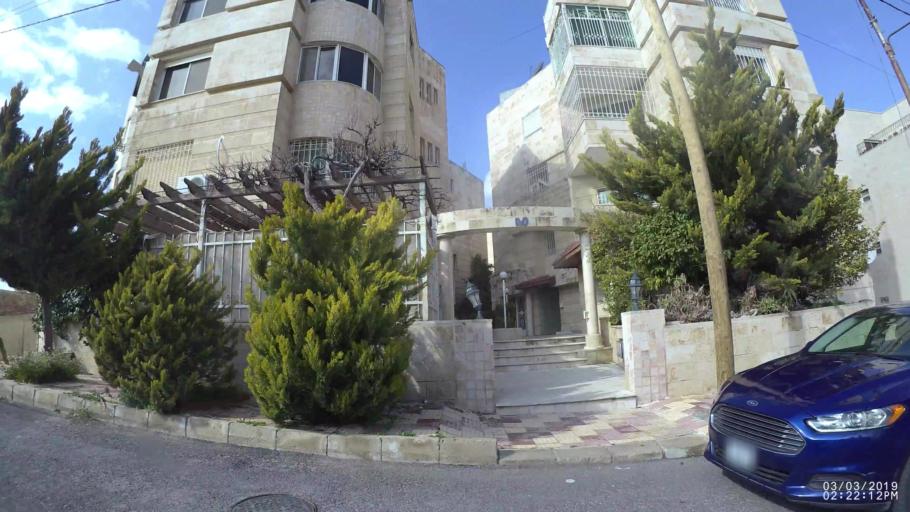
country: JO
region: Amman
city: Amman
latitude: 31.9708
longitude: 35.8889
